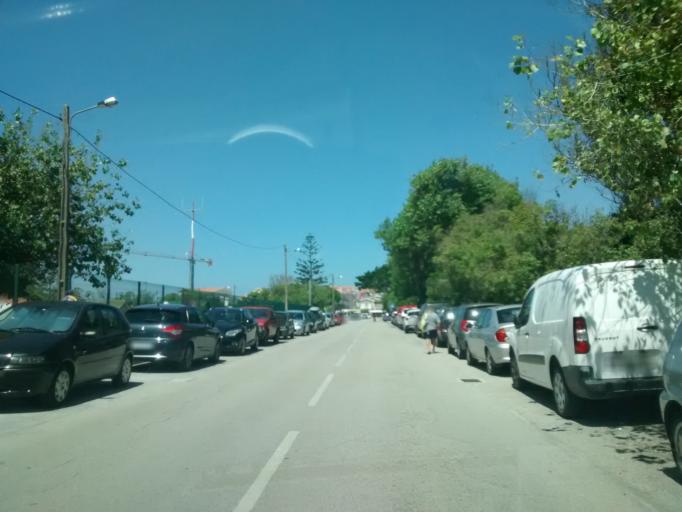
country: PT
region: Coimbra
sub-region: Mira
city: Mira
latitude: 40.4496
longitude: -8.8011
